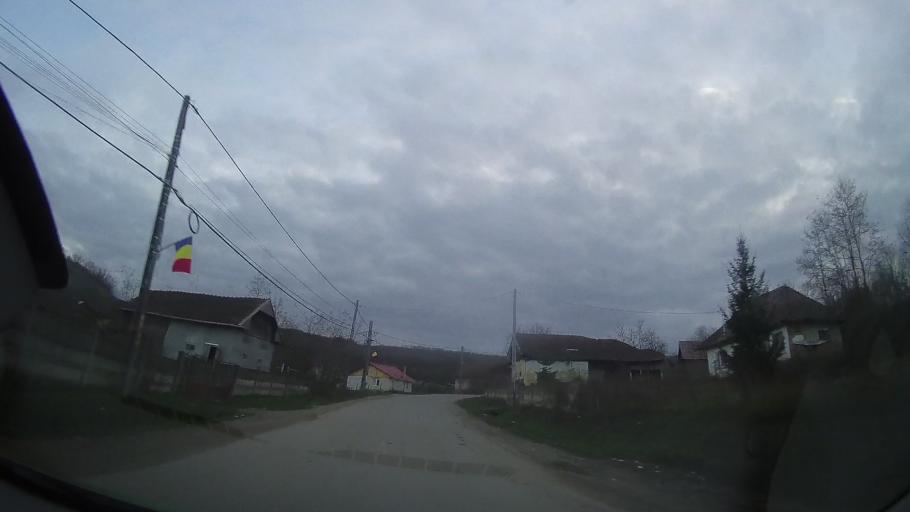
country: RO
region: Cluj
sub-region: Comuna Palatca
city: Palatca
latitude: 46.8383
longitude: 23.9835
